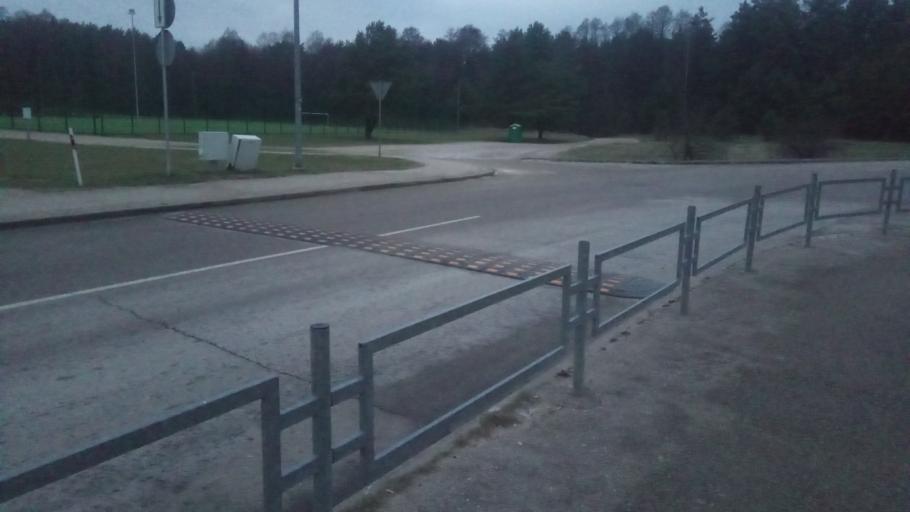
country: LV
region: Daugavpils
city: Daugavpils
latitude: 55.8678
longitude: 26.5842
